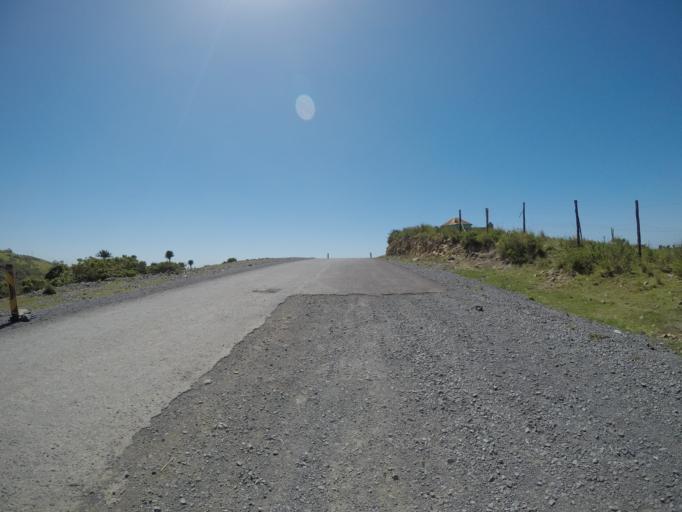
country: ZA
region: Eastern Cape
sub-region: OR Tambo District Municipality
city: Libode
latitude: -31.9934
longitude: 29.1324
